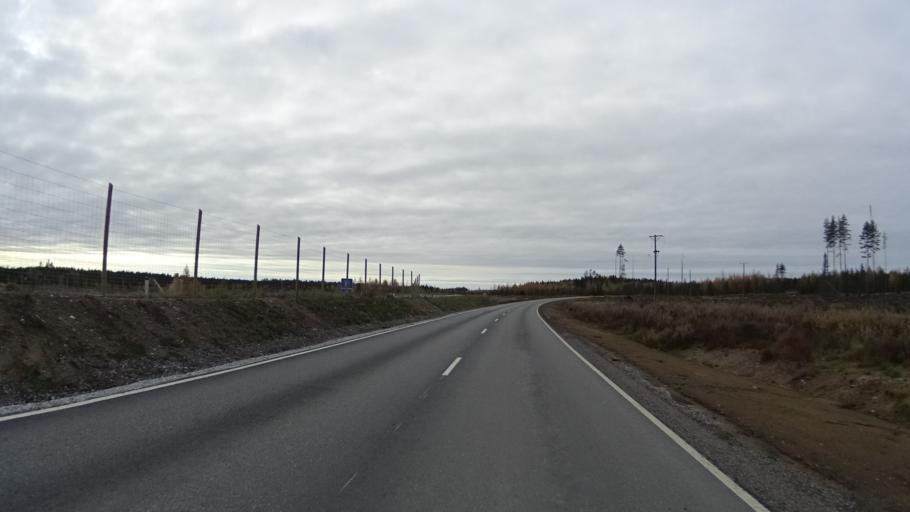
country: FI
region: South Karelia
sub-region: Lappeenranta
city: Lemi
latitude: 60.9982
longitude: 27.9361
